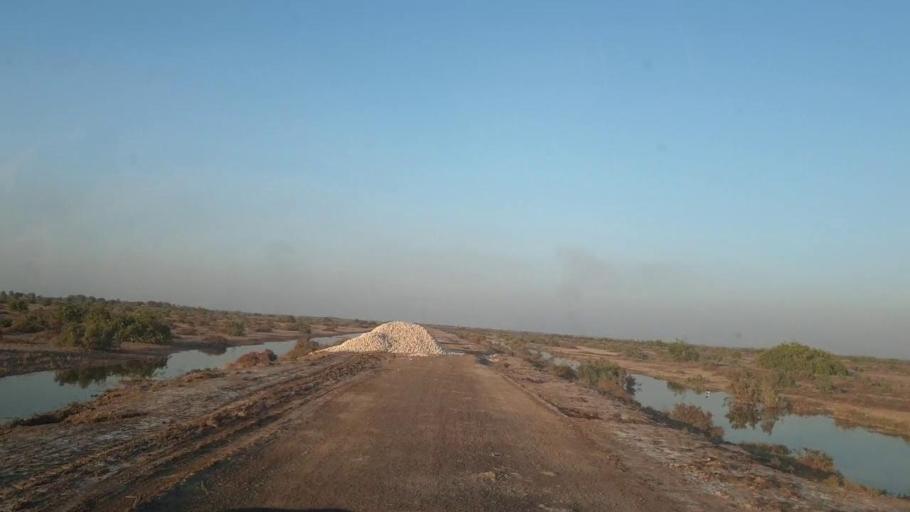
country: PK
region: Sindh
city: Mirpur Khas
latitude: 25.4367
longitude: 69.0764
